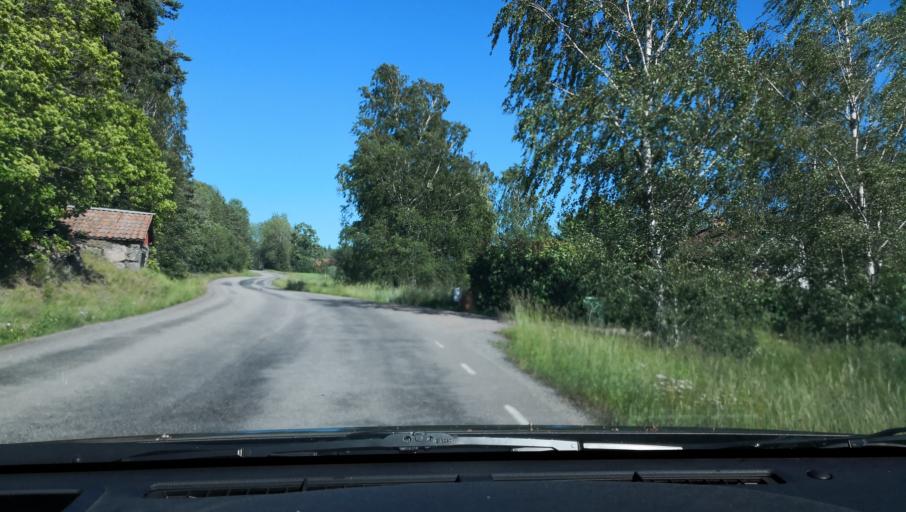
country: SE
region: Soedermanland
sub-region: Eskilstuna Kommun
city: Arla
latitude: 59.3232
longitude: 16.6171
